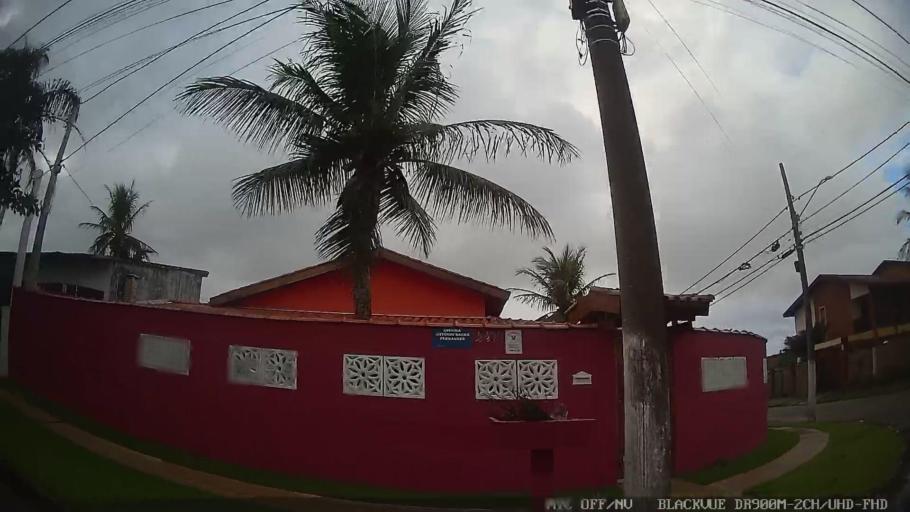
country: BR
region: Sao Paulo
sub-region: Itanhaem
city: Itanhaem
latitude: -24.2152
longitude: -46.8496
